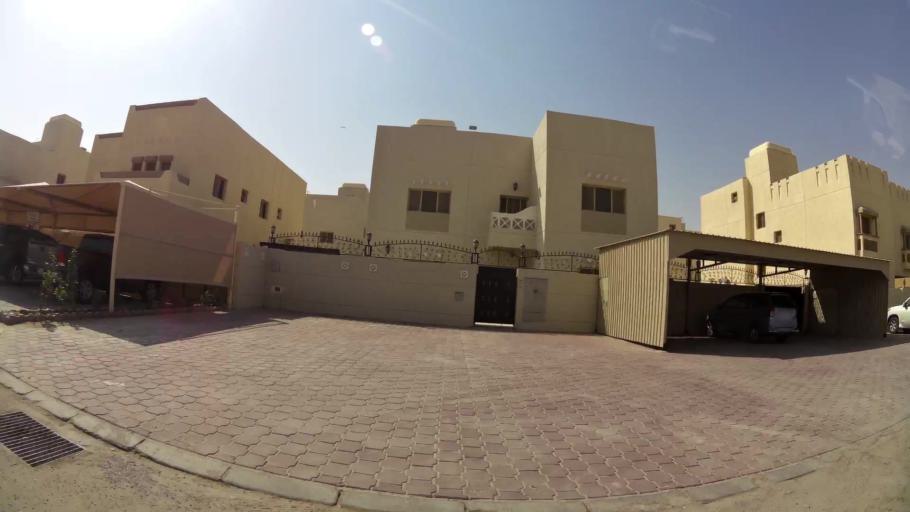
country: KW
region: Al Ahmadi
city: Al Wafrah
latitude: 28.8094
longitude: 48.0499
